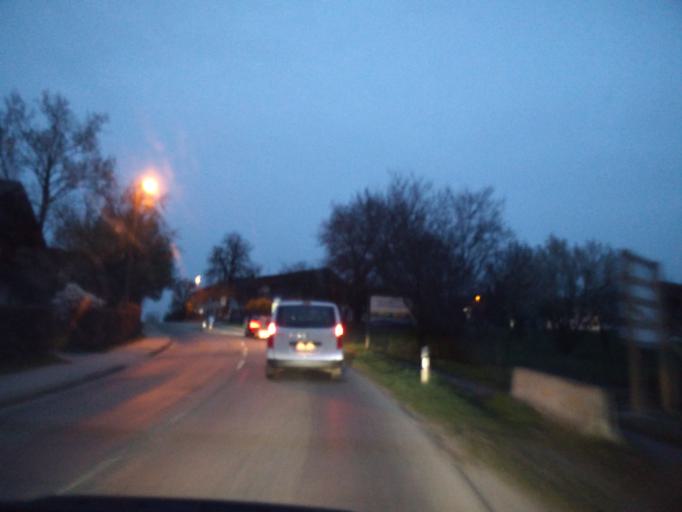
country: DE
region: Bavaria
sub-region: Upper Bavaria
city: Edling
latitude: 48.0585
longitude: 12.1853
